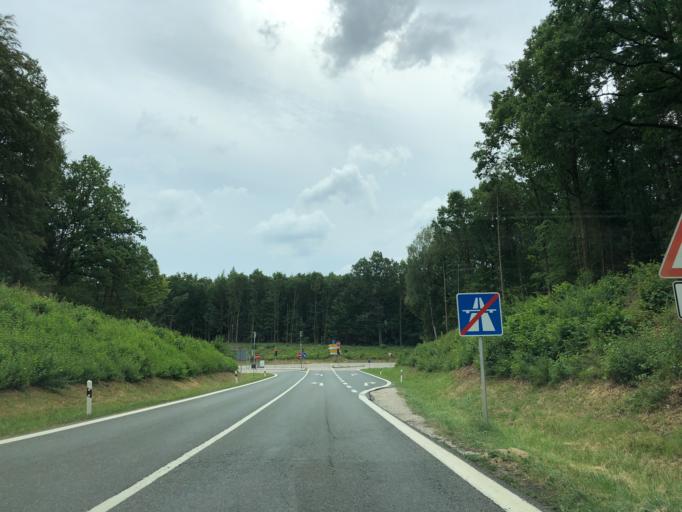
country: DE
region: Bavaria
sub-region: Regierungsbezirk Mittelfranken
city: Obermichelbach
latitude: 49.5666
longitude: 10.9413
